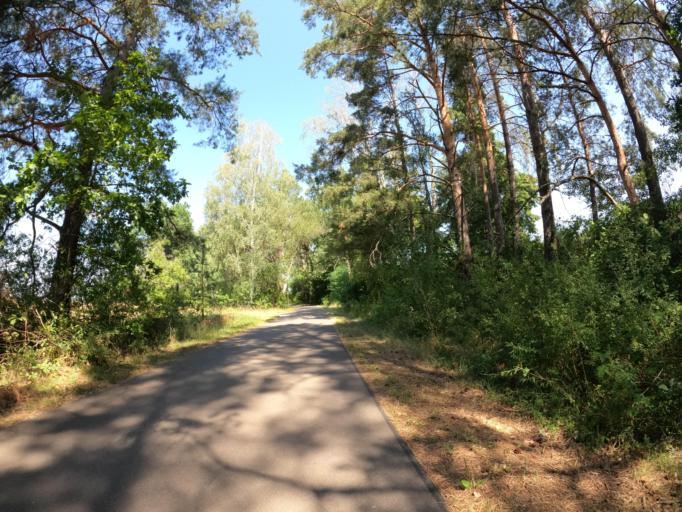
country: DE
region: Brandenburg
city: Templin
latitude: 53.1739
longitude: 13.5161
